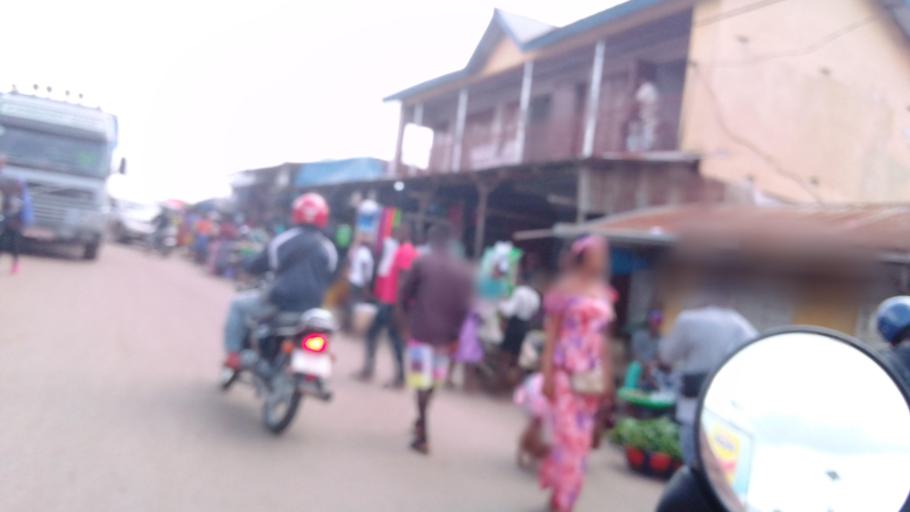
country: SL
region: Northern Province
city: Makeni
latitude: 8.8875
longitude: -12.0426
